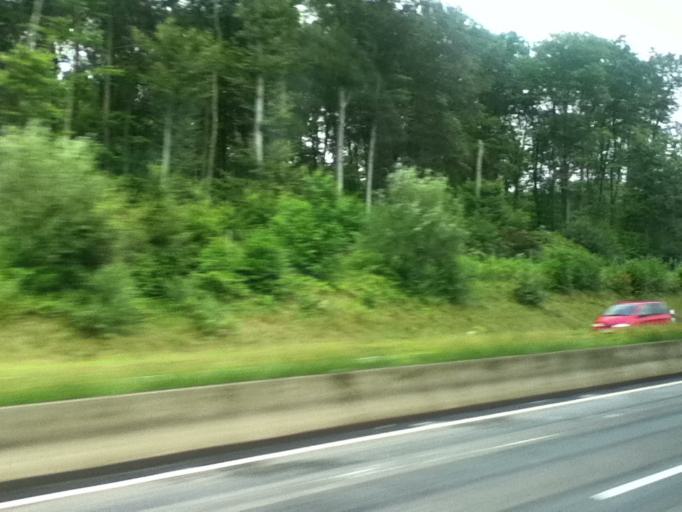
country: DE
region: Hesse
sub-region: Regierungsbezirk Giessen
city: Grunberg
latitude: 50.6394
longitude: 8.9542
